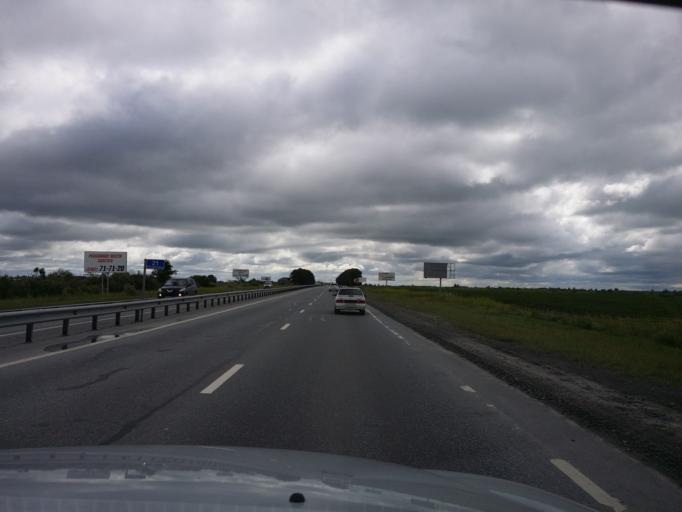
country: RU
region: Tjumen
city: Antipino
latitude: 57.1591
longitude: 65.8211
